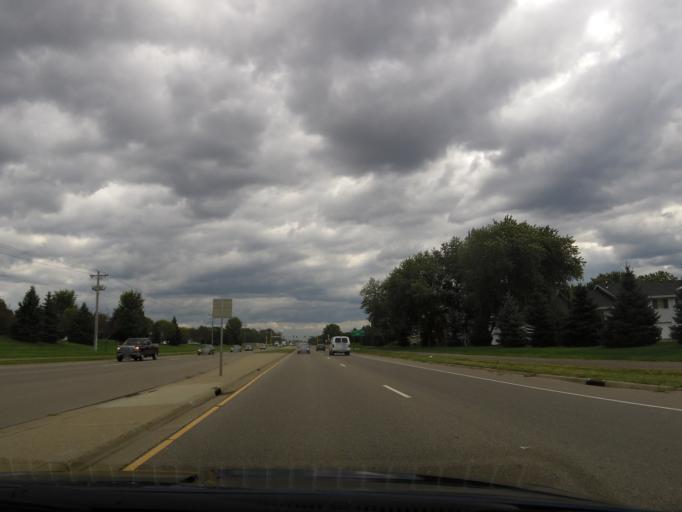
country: US
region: Minnesota
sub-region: Dakota County
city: Apple Valley
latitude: 44.7174
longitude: -93.2016
